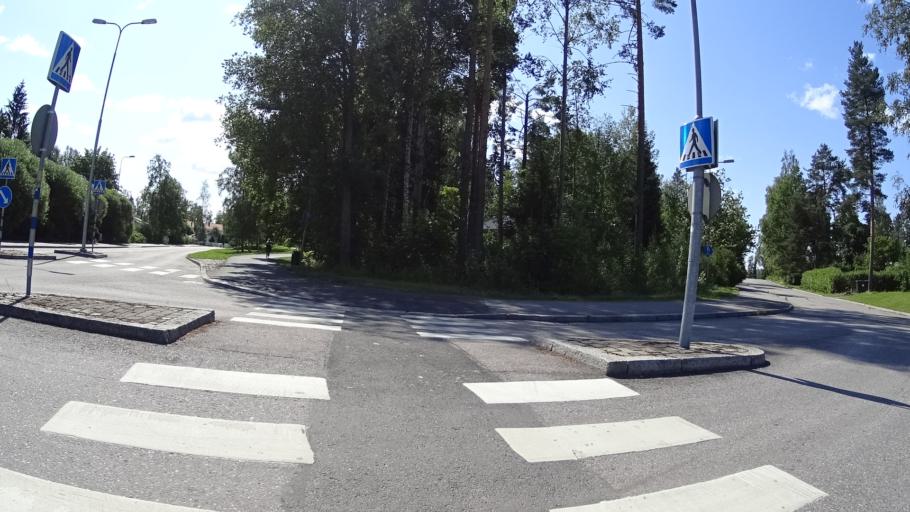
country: FI
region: Uusimaa
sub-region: Helsinki
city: Jaervenpaeae
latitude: 60.4793
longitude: 25.0720
